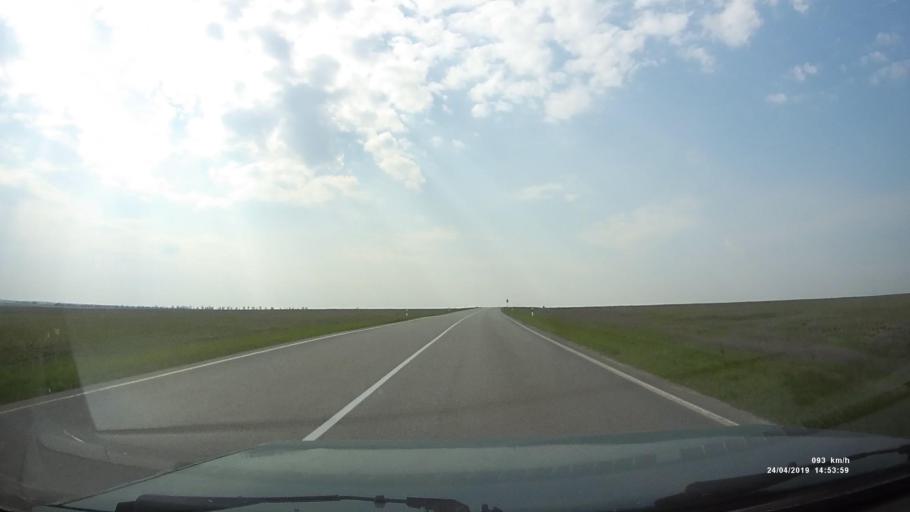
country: RU
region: Rostov
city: Remontnoye
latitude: 46.5321
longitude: 43.6475
